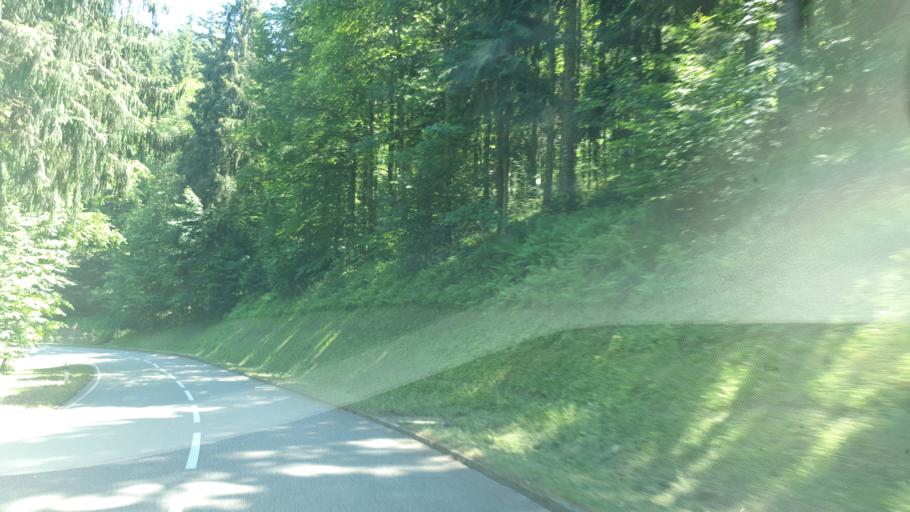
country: DE
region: Baden-Wuerttemberg
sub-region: Freiburg Region
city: Horben
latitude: 47.9182
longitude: 7.8797
